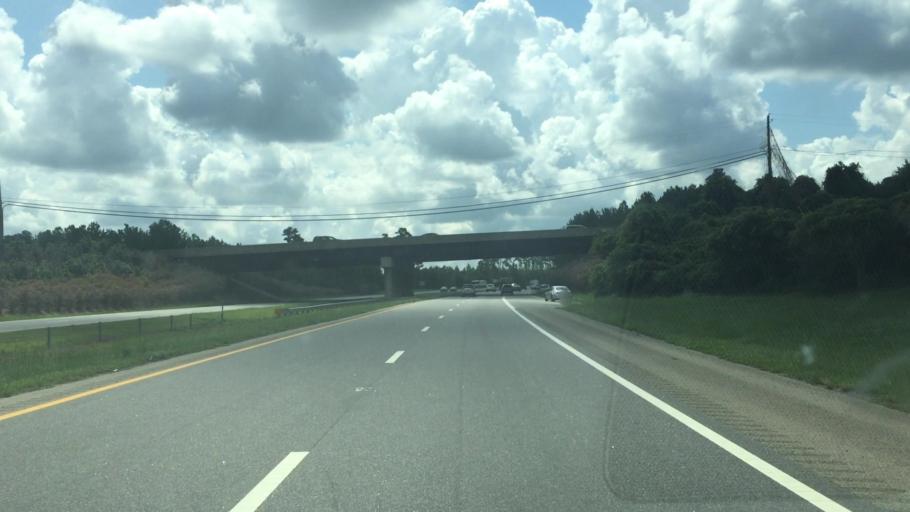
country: US
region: North Carolina
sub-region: Richmond County
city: Cordova
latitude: 34.9117
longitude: -79.7930
